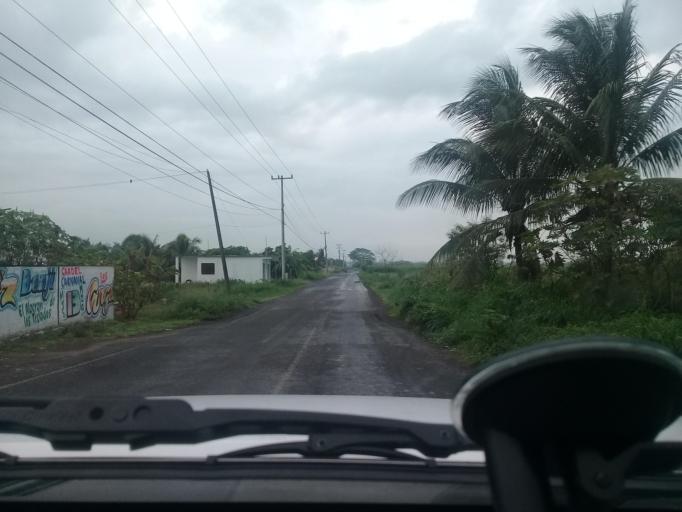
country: MX
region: Veracruz
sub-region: La Antigua
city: Nicolas Blanco (San Pancho)
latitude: 19.3519
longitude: -96.3441
